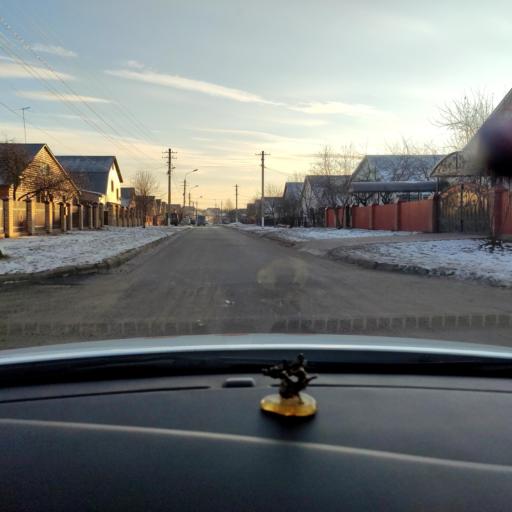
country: RU
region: Tatarstan
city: Stolbishchi
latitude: 55.6112
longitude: 49.1367
